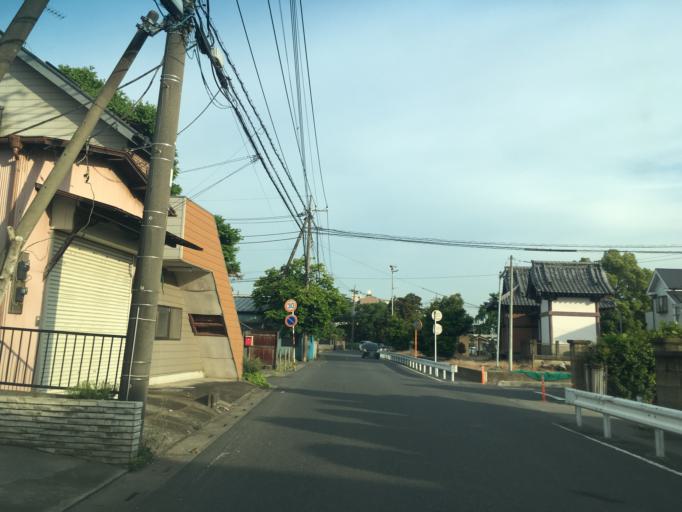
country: JP
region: Saitama
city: Yoshikawa
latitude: 35.8677
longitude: 139.8184
